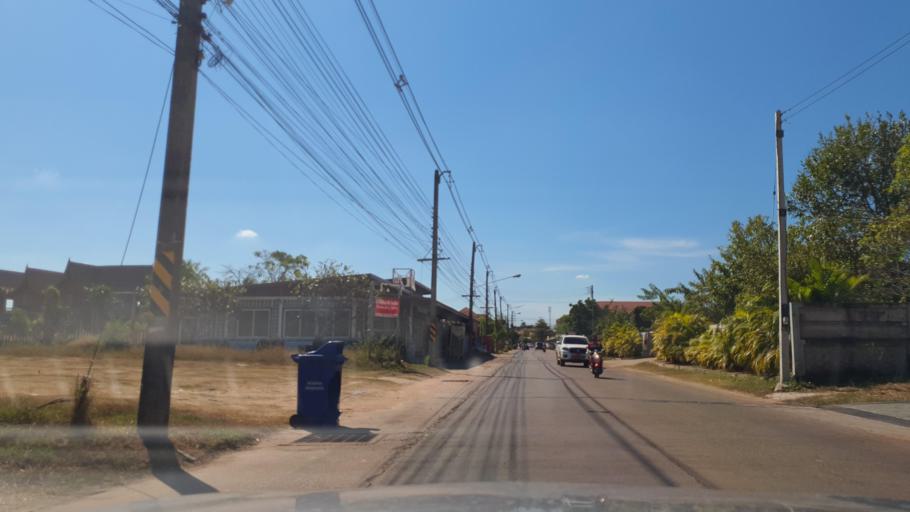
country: TH
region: Sakon Nakhon
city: Sakon Nakhon
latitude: 17.1617
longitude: 104.1226
